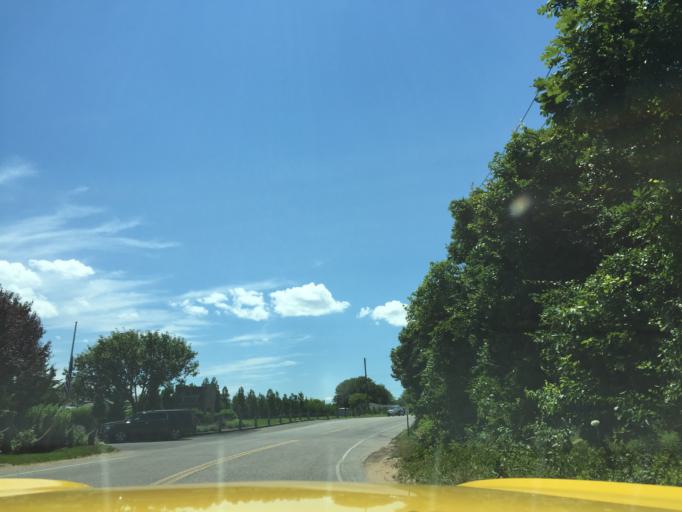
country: US
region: New York
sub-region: Suffolk County
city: Montauk
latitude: 41.0167
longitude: -71.9911
